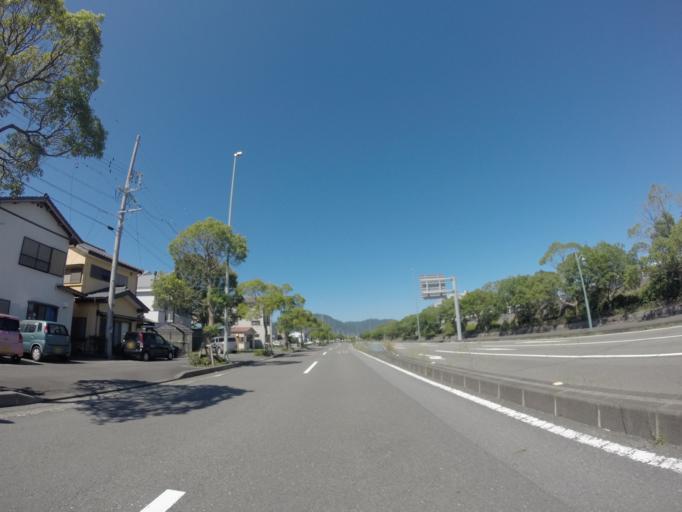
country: JP
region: Shizuoka
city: Yaizu
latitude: 34.8573
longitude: 138.3245
